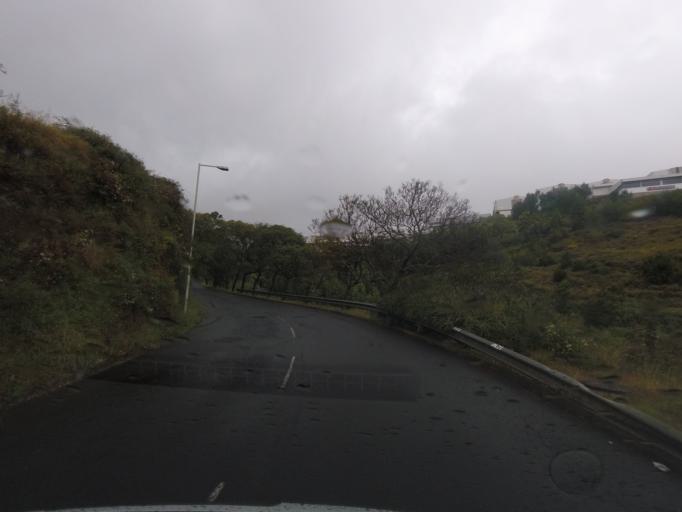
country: PT
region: Madeira
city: Canico
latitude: 32.6487
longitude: -16.8602
